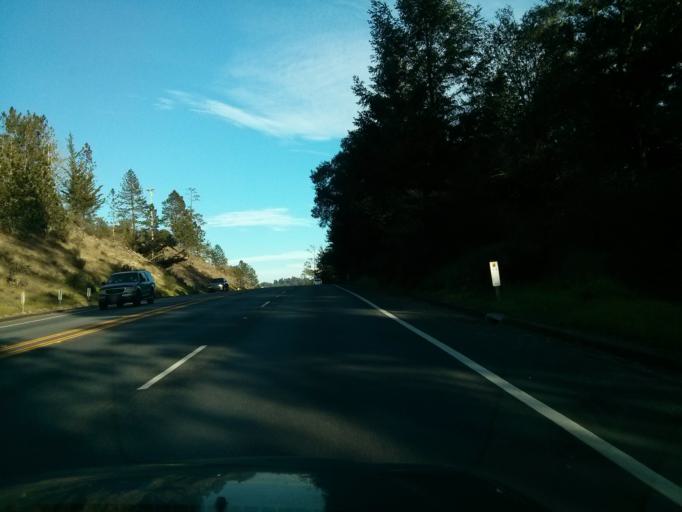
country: US
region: California
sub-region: Santa Cruz County
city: Mount Hermon
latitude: 37.0548
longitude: -122.0536
